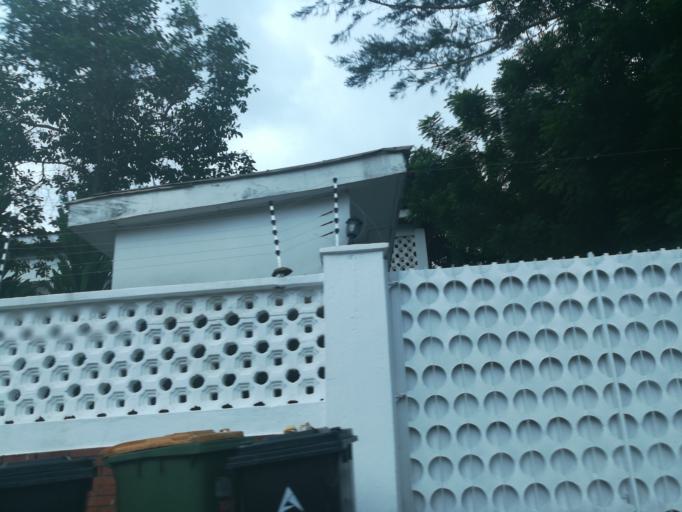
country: NG
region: Lagos
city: Ikeja
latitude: 6.6171
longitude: 3.3480
